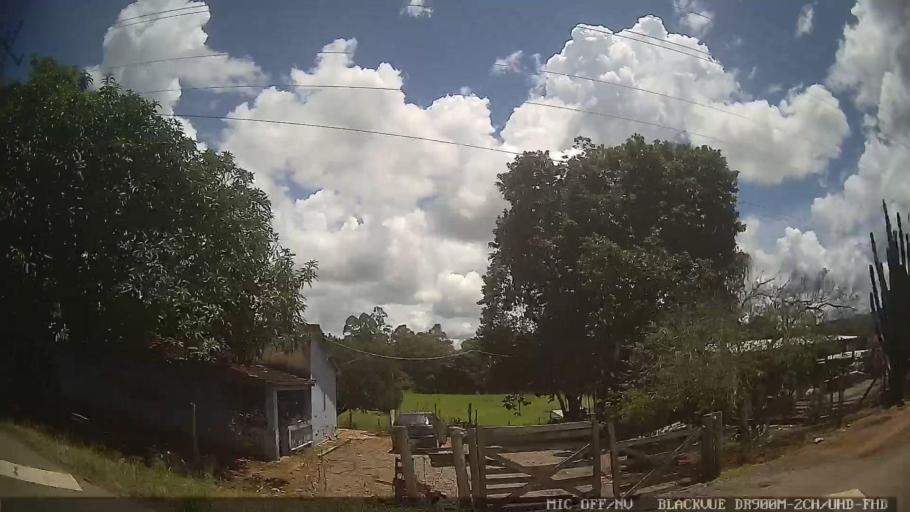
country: BR
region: Sao Paulo
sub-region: Braganca Paulista
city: Braganca Paulista
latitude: -22.8810
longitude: -46.6090
